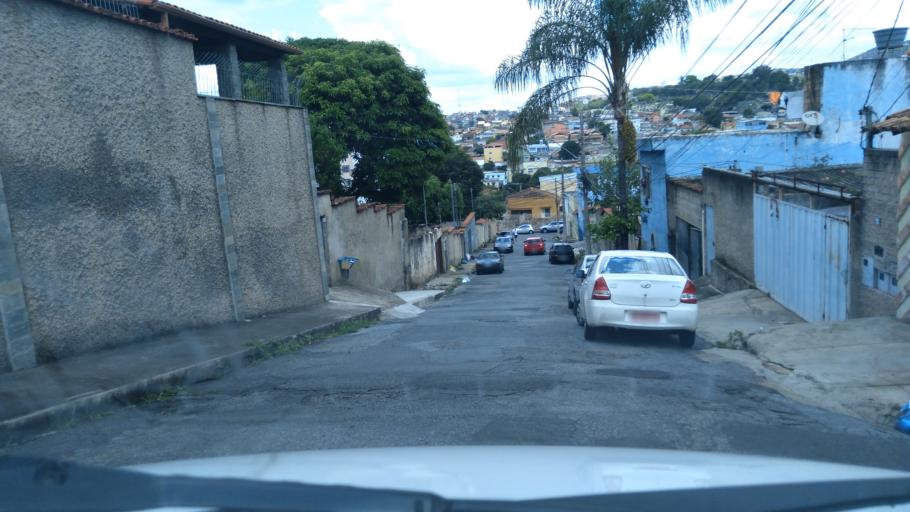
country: BR
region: Minas Gerais
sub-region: Belo Horizonte
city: Belo Horizonte
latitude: -19.9175
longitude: -43.9047
